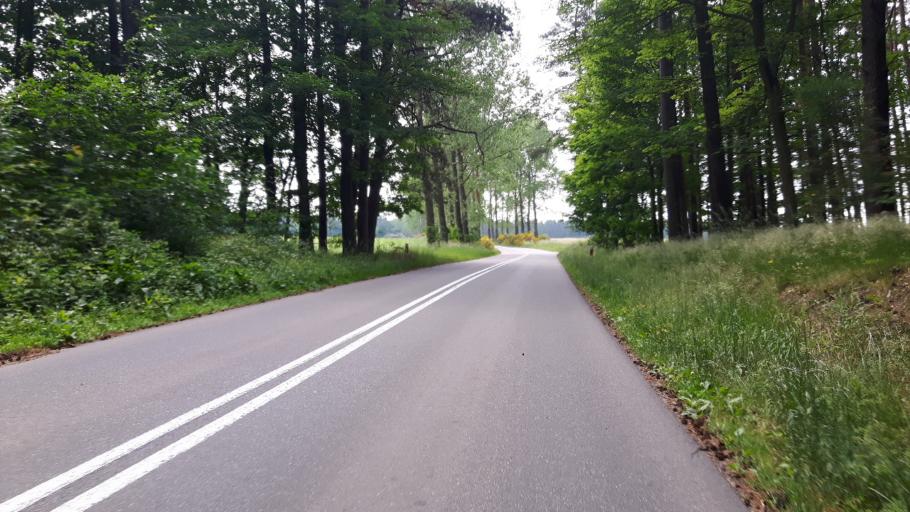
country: PL
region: Pomeranian Voivodeship
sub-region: Powiat leborski
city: Leba
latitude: 54.7494
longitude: 17.7114
